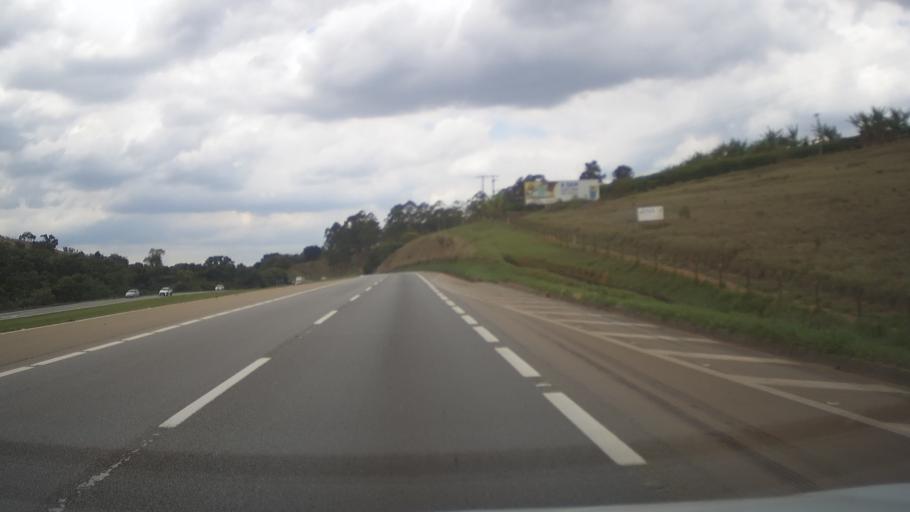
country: BR
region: Minas Gerais
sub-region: Tres Coracoes
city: Tres Coracoes
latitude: -21.5259
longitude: -45.2268
